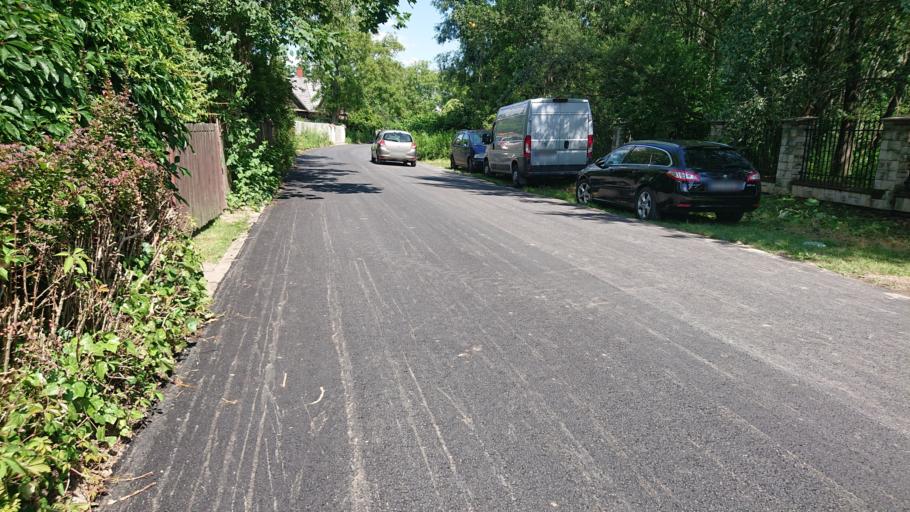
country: PL
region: Lublin Voivodeship
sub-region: Powiat pulawski
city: Kazimierz Dolny
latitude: 51.3236
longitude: 21.9590
